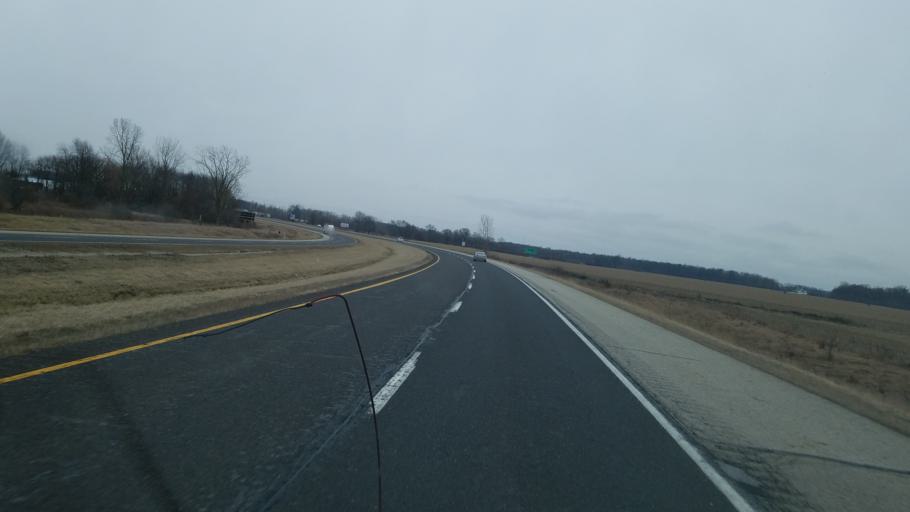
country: US
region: Indiana
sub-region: Fulton County
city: Rochester
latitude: 41.0536
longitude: -86.2395
